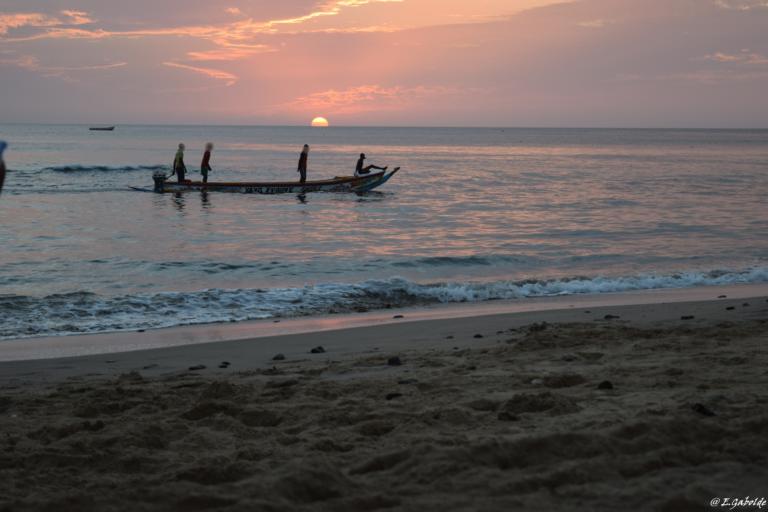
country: SN
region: Dakar
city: Mermoz Boabab
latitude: 14.7235
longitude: -17.4953
